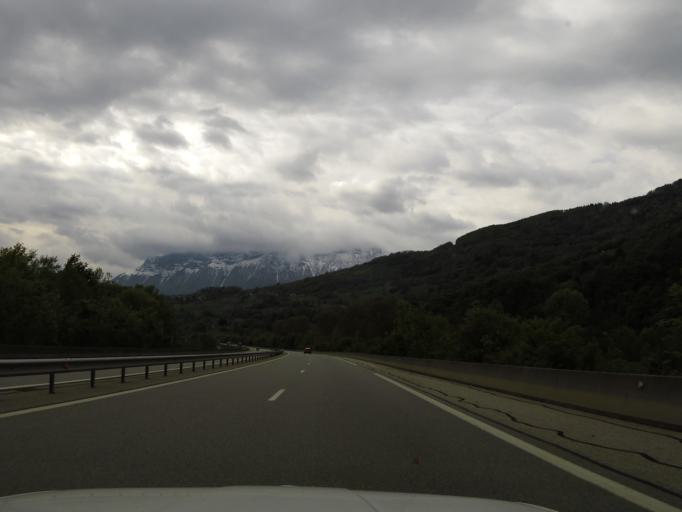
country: FR
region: Rhone-Alpes
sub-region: Departement de la Savoie
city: Aiton
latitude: 45.5543
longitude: 6.2900
